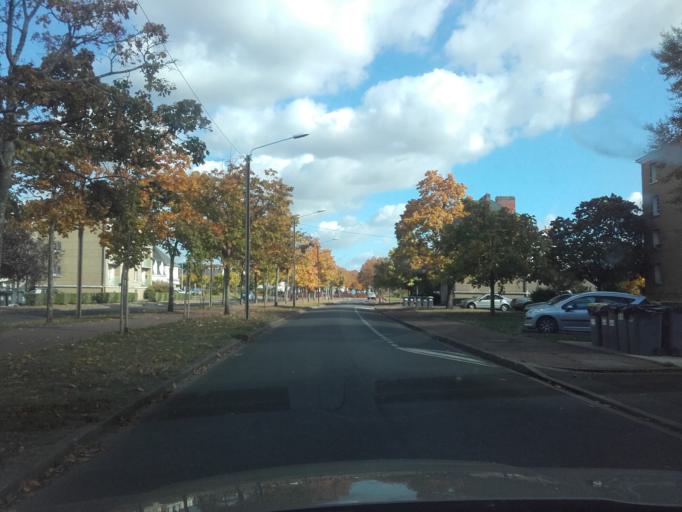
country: FR
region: Centre
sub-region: Departement d'Indre-et-Loire
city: Saint-Pierre-des-Corps
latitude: 47.3913
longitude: 0.7310
